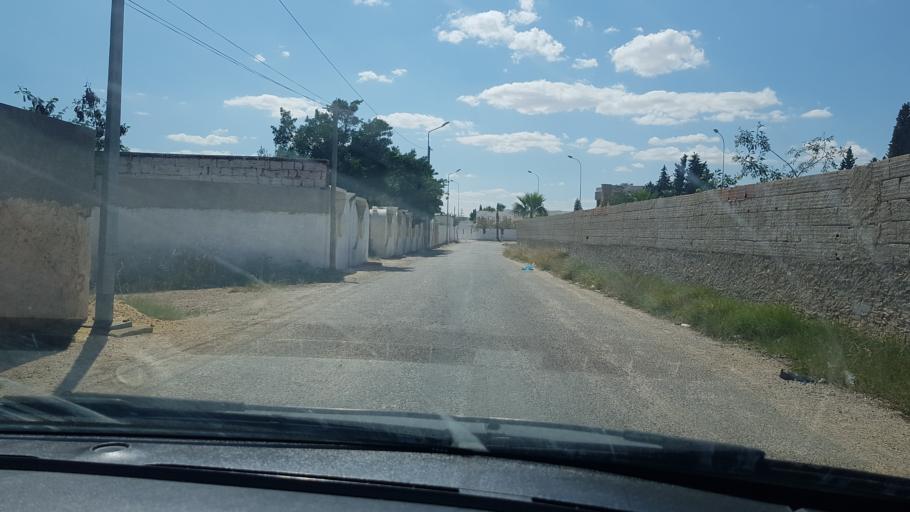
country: TN
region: Safaqis
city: Al Qarmadah
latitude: 34.8288
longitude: 10.7613
